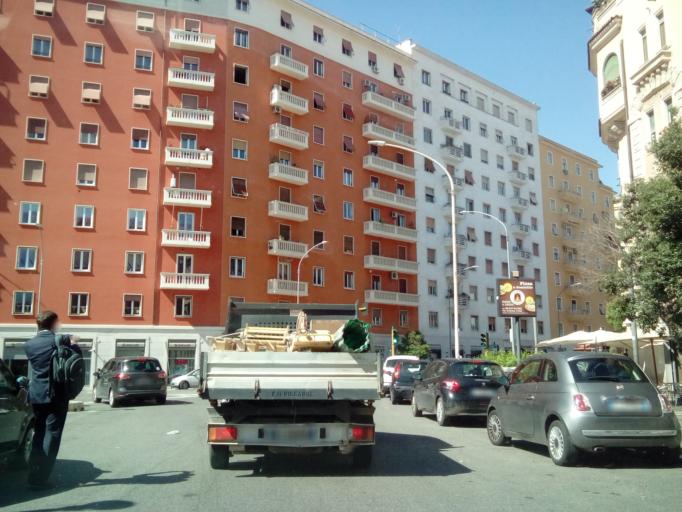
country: IT
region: Latium
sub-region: Citta metropolitana di Roma Capitale
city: Rome
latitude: 41.8803
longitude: 12.5085
